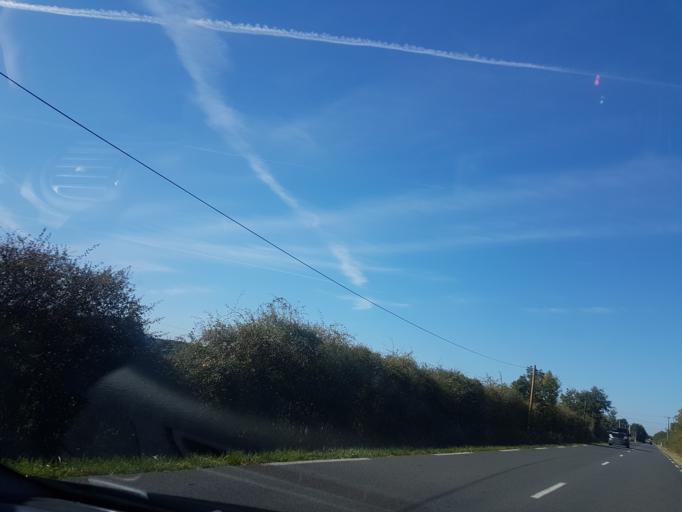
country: FR
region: Pays de la Loire
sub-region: Departement de la Loire-Atlantique
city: Casson
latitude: 47.4279
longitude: -1.5895
